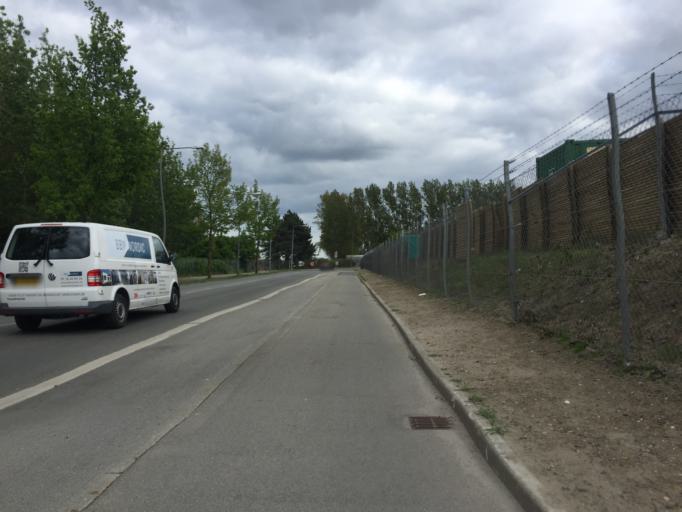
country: DK
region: Capital Region
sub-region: Kobenhavn
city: Christianshavn
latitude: 55.6780
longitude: 12.6180
